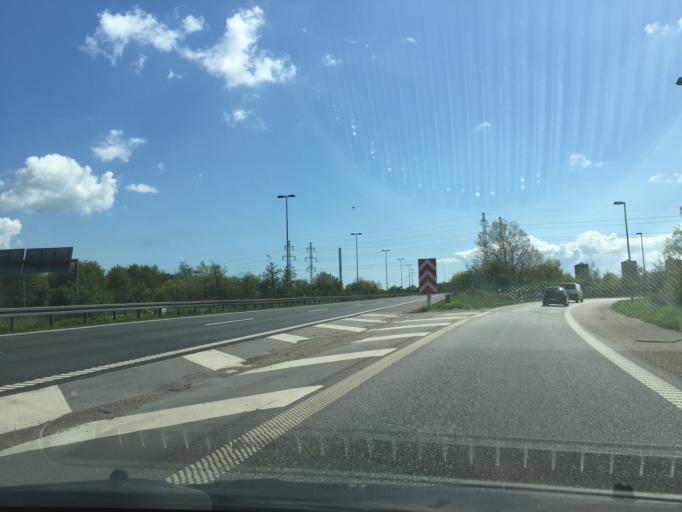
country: DK
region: Capital Region
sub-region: Brondby Kommune
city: Brondbyvester
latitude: 55.6331
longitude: 12.4281
